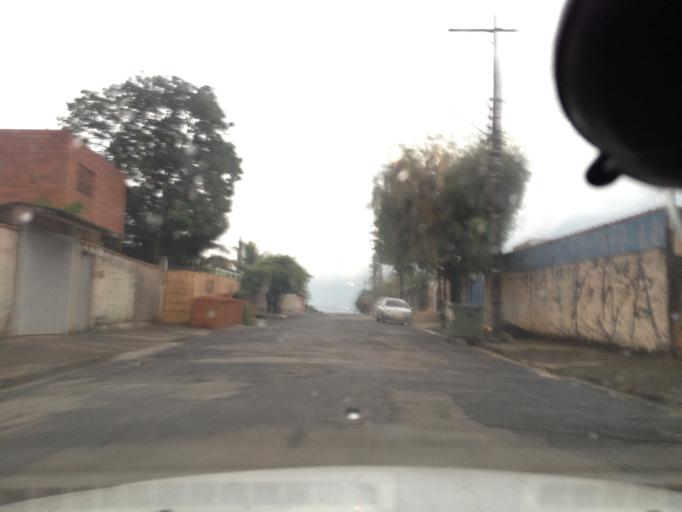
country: BR
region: Sao Paulo
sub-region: Salto
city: Salto
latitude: -23.1931
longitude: -47.2677
